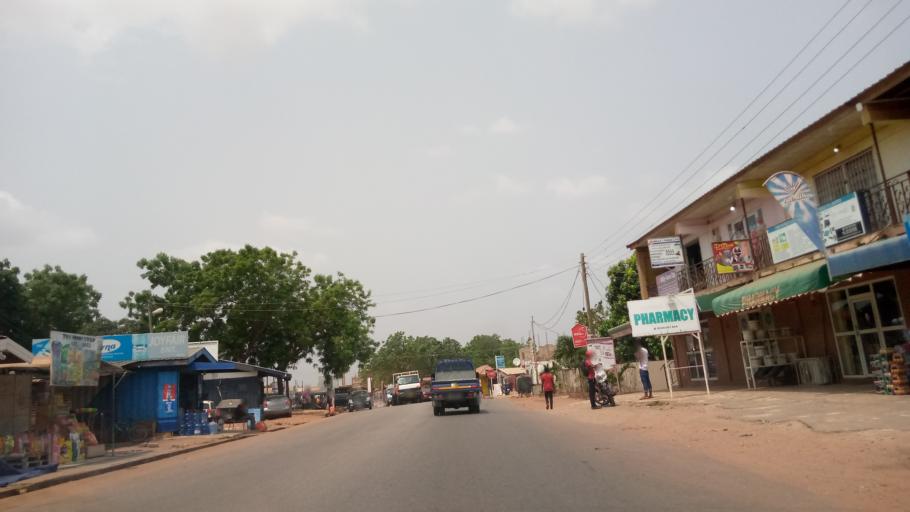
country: GH
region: Greater Accra
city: Medina Estates
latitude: 5.6869
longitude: -0.1936
